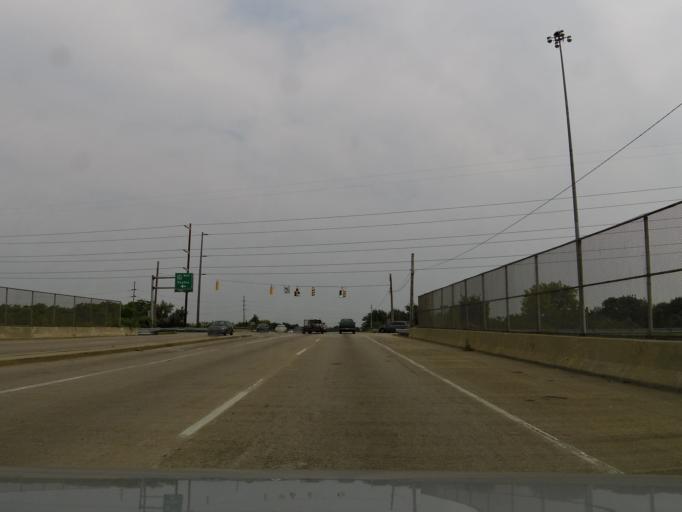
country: US
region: Ohio
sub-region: Montgomery County
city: Riverside
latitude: 39.7456
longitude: -84.1206
